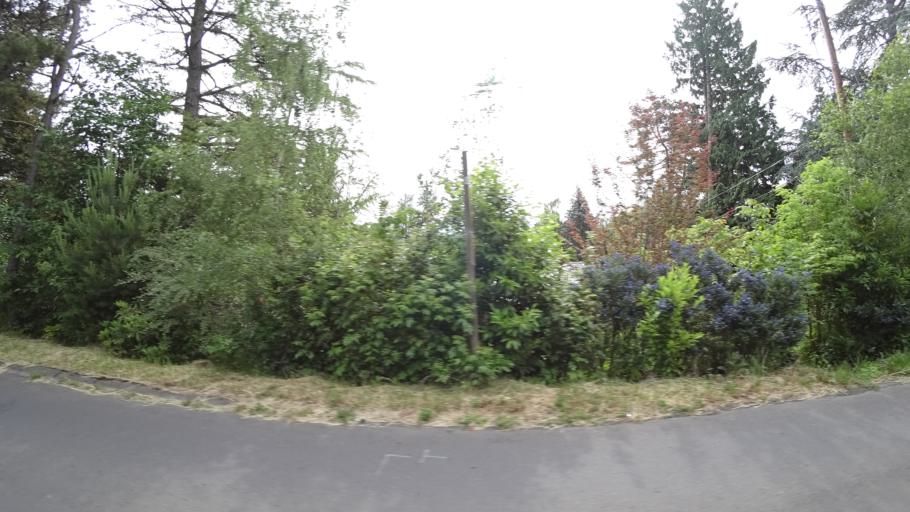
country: US
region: Oregon
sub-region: Clackamas County
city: Lake Oswego
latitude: 45.4306
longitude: -122.6923
